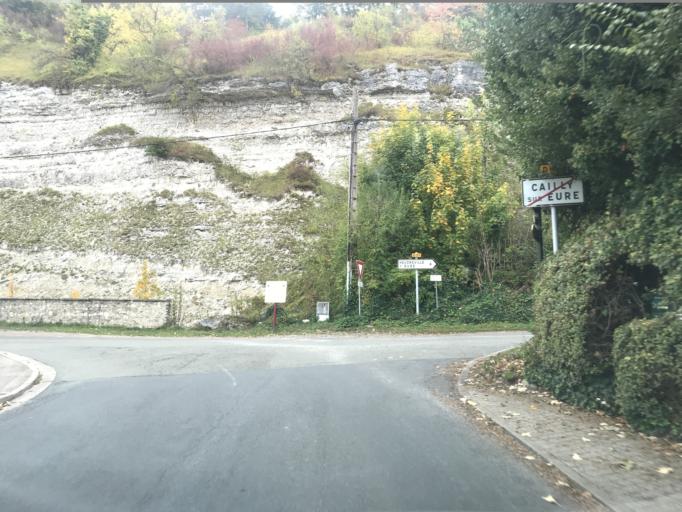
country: FR
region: Haute-Normandie
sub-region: Departement de l'Eure
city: Heudreville-sur-Eure
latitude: 49.1147
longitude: 1.2078
